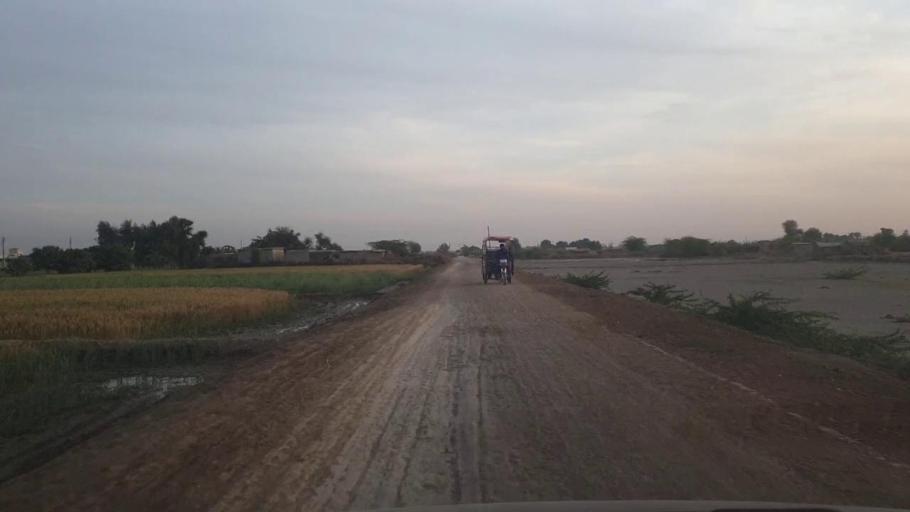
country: PK
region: Sindh
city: Kunri
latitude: 25.2259
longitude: 69.5550
